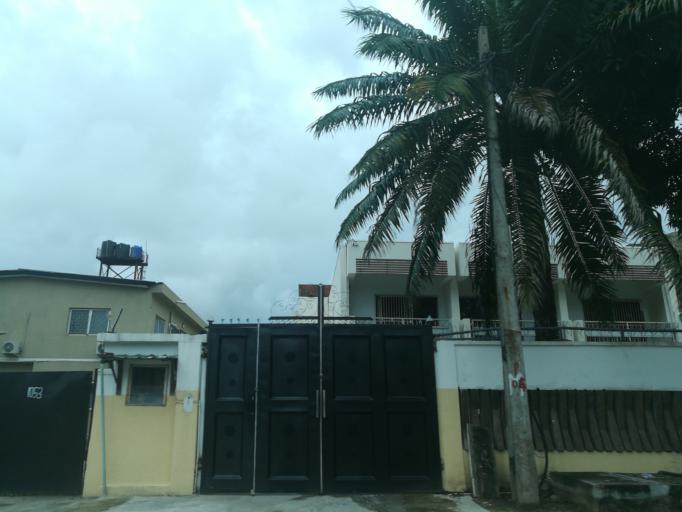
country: NG
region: Lagos
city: Ikoyi
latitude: 6.4289
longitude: 3.4175
